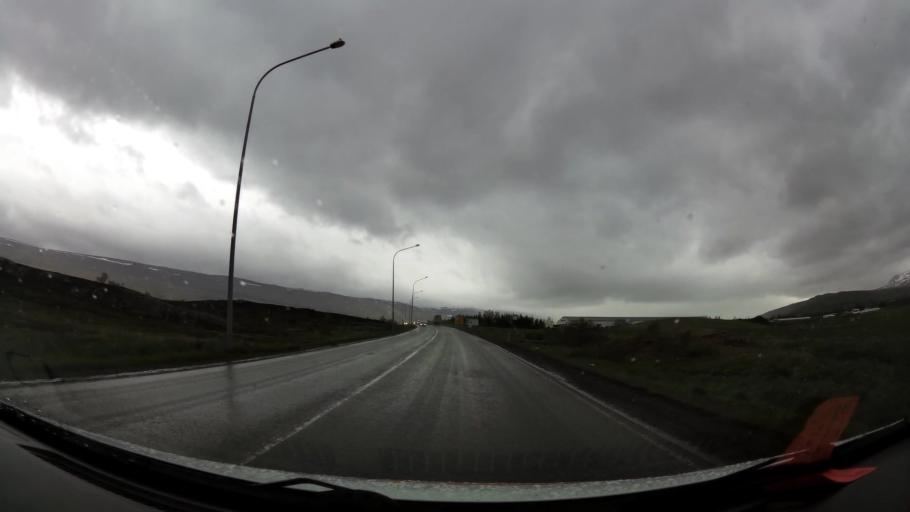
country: IS
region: Northeast
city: Akureyri
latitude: 65.7019
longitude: -18.1487
